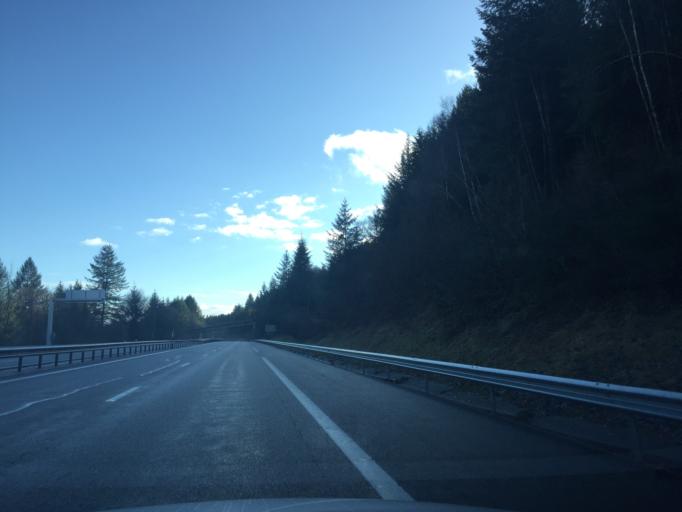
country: FR
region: Auvergne
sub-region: Departement du Puy-de-Dome
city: Chabreloche
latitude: 45.8541
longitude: 3.7258
